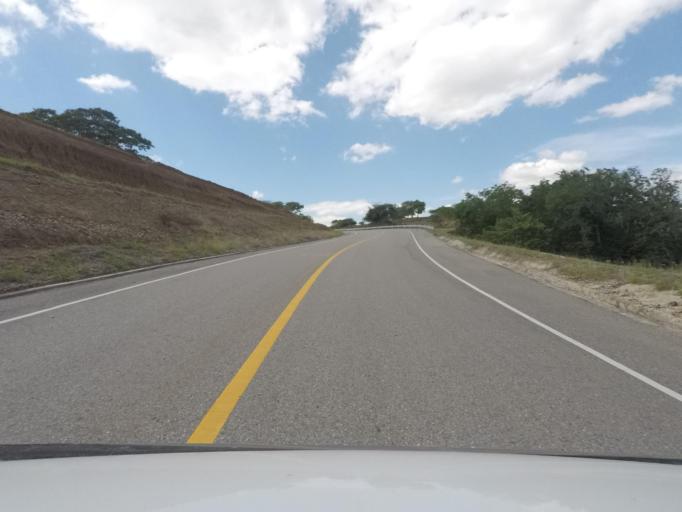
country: TL
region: Lautem
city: Lospalos
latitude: -8.4043
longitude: 126.8185
